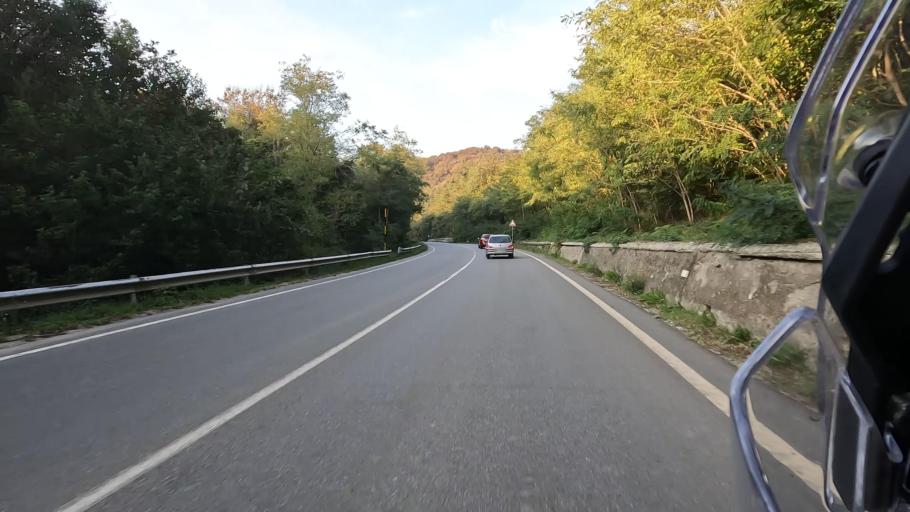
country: IT
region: Liguria
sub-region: Provincia di Savona
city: Osteria dei Cacciatori-Stella
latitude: 44.4409
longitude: 8.4842
